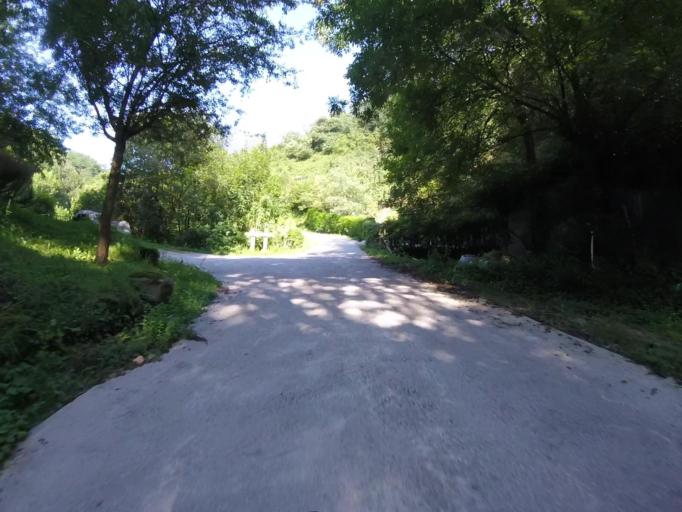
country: ES
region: Basque Country
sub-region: Provincia de Guipuzcoa
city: Astigarraga
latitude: 43.2389
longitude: -1.9326
